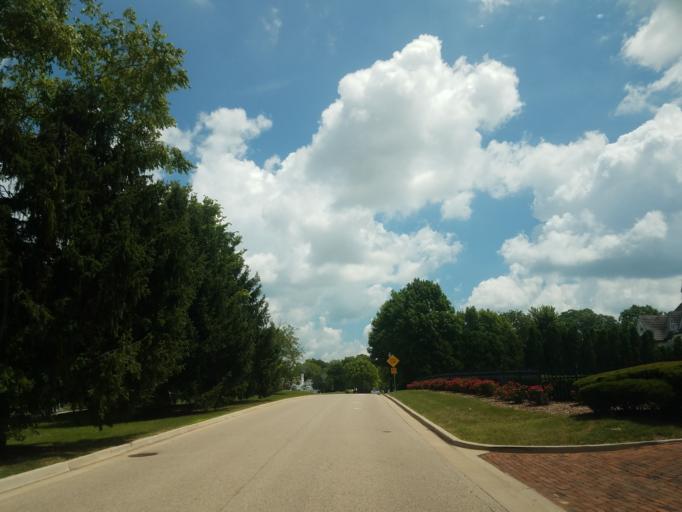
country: US
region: Illinois
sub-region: McLean County
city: Bloomington
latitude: 40.4820
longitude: -88.9676
